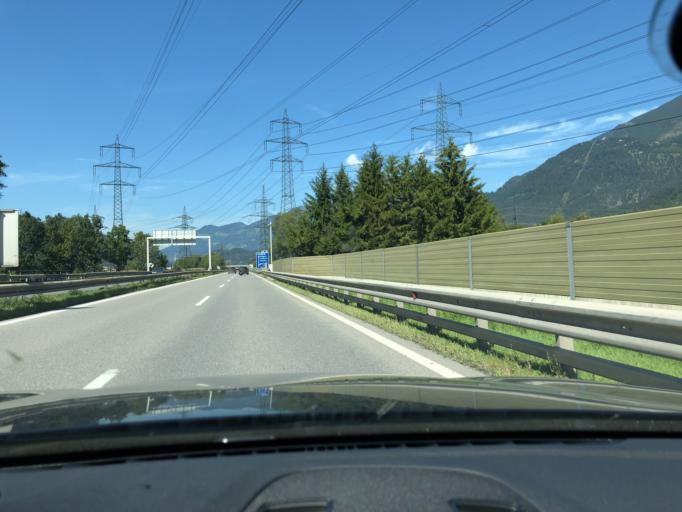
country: AT
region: Vorarlberg
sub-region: Politischer Bezirk Bludenz
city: Bludenz
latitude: 47.1403
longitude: 9.8256
